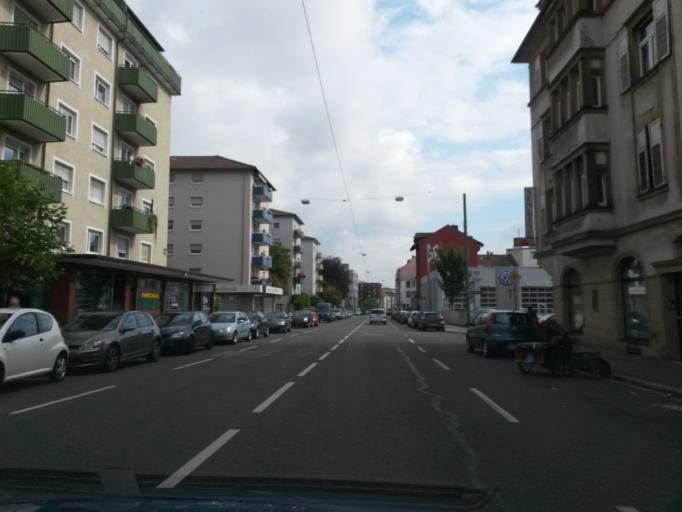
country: DE
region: Baden-Wuerttemberg
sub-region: Karlsruhe Region
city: Pforzheim
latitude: 48.8915
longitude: 8.6807
